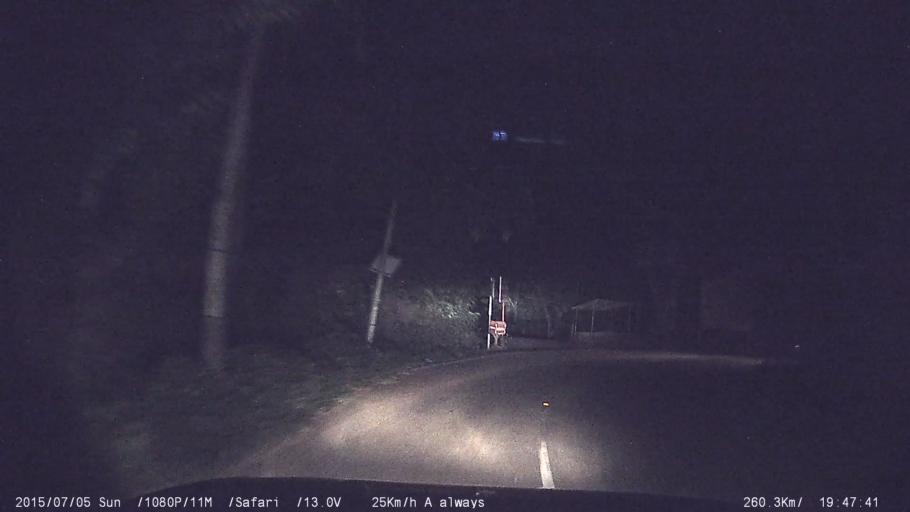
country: IN
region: Kerala
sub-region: Palakkad district
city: Palakkad
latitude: 10.7823
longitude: 76.5537
